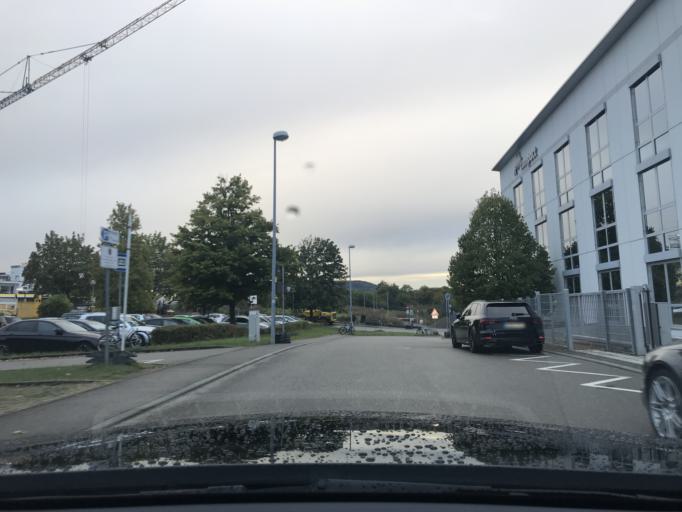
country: DE
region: Baden-Wuerttemberg
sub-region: Regierungsbezirk Stuttgart
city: Weinstadt-Endersbach
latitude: 48.8127
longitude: 9.3530
